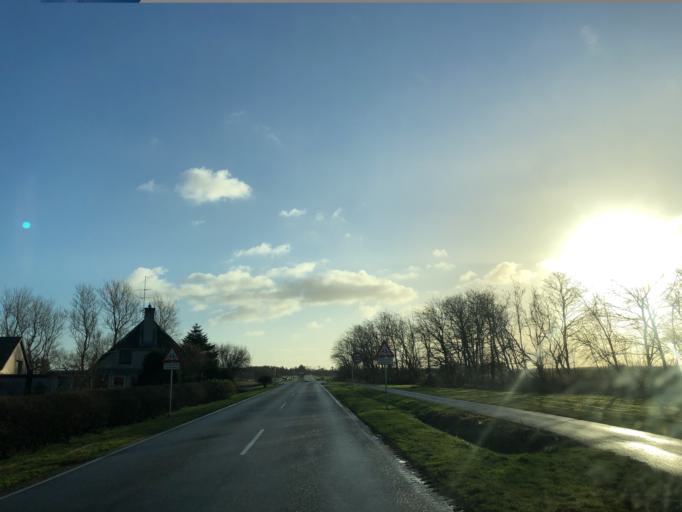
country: DK
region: Central Jutland
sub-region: Holstebro Kommune
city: Ulfborg
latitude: 56.2046
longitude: 8.2589
